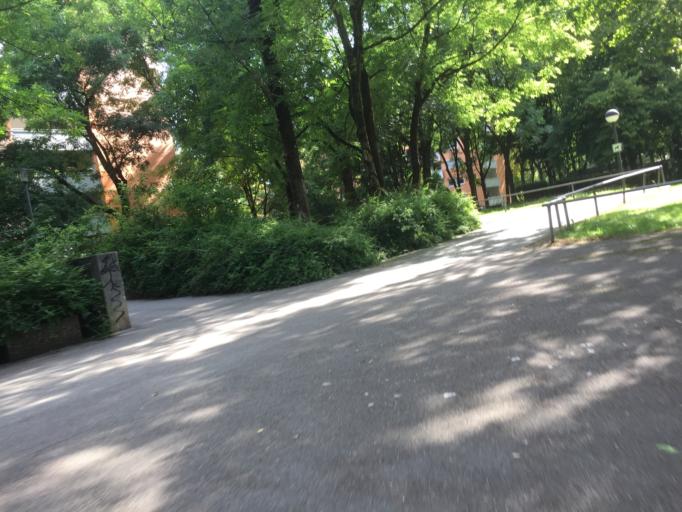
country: DE
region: Bavaria
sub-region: Upper Bavaria
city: Neubiberg
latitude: 48.1076
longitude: 11.6339
